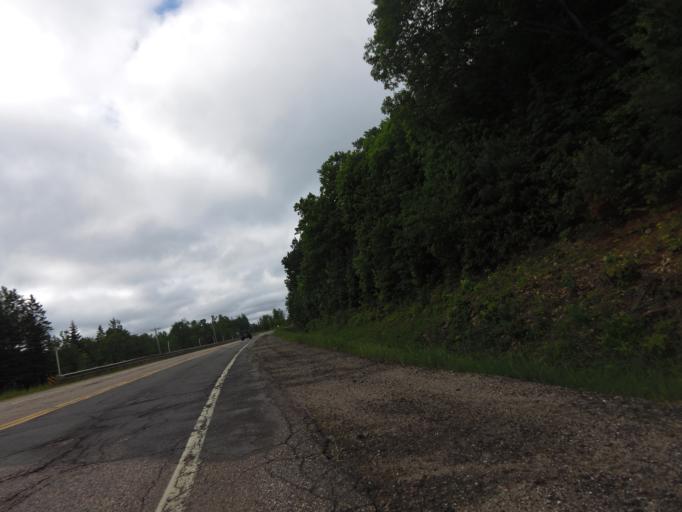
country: CA
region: Quebec
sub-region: Outaouais
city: Shawville
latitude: 45.8282
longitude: -76.4606
